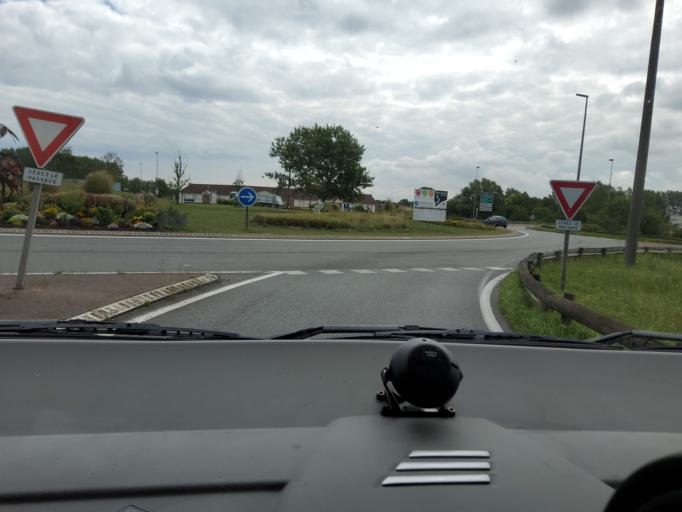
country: FR
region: Nord-Pas-de-Calais
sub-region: Departement du Nord
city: Loon-Plage
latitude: 50.9952
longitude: 2.2002
